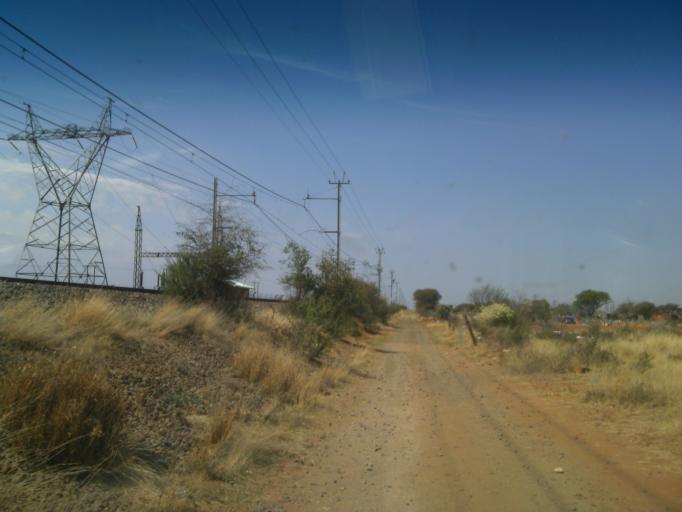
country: ZA
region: Northern Cape
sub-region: Frances Baard District Municipality
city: Barkly West
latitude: -28.5174
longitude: 24.4995
